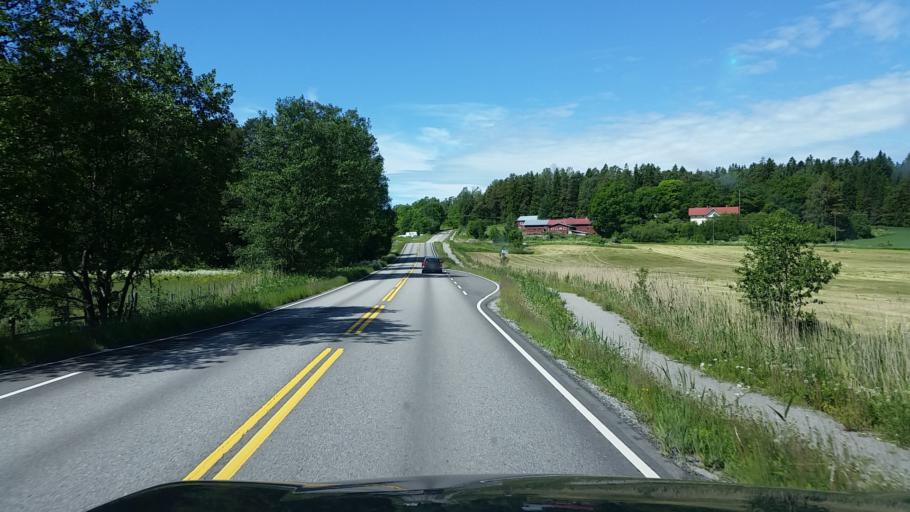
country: FI
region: Varsinais-Suomi
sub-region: Aboland-Turunmaa
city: Laensi-Turunmaa
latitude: 60.2446
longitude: 22.1995
